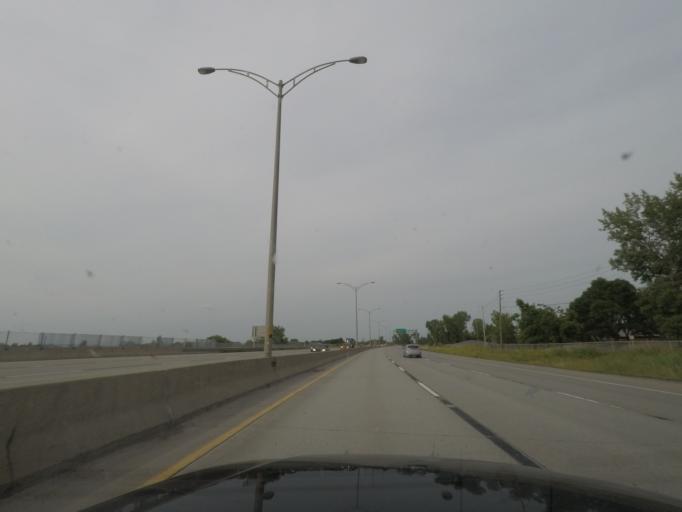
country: CA
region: Quebec
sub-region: Monteregie
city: La Prairie
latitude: 45.4230
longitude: -73.4960
